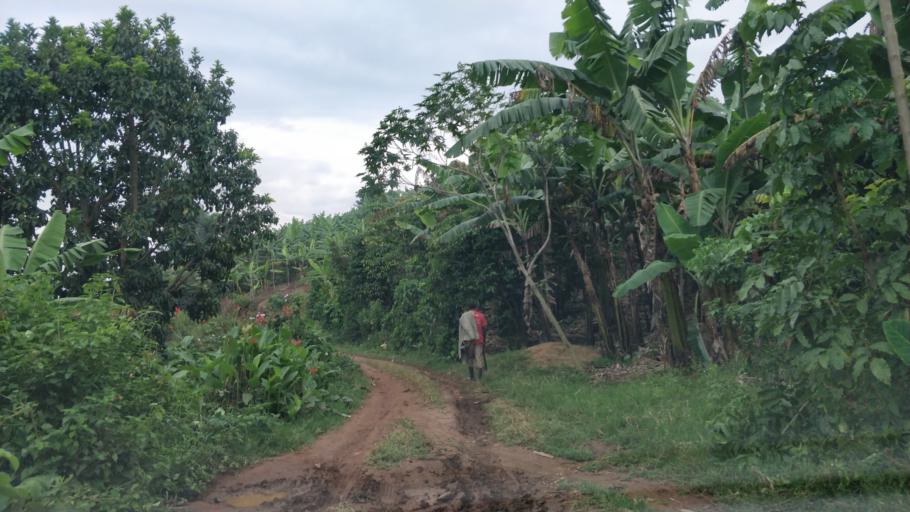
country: UG
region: Western Region
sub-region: Sheema District
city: Kibingo
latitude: -0.7025
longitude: 30.3980
